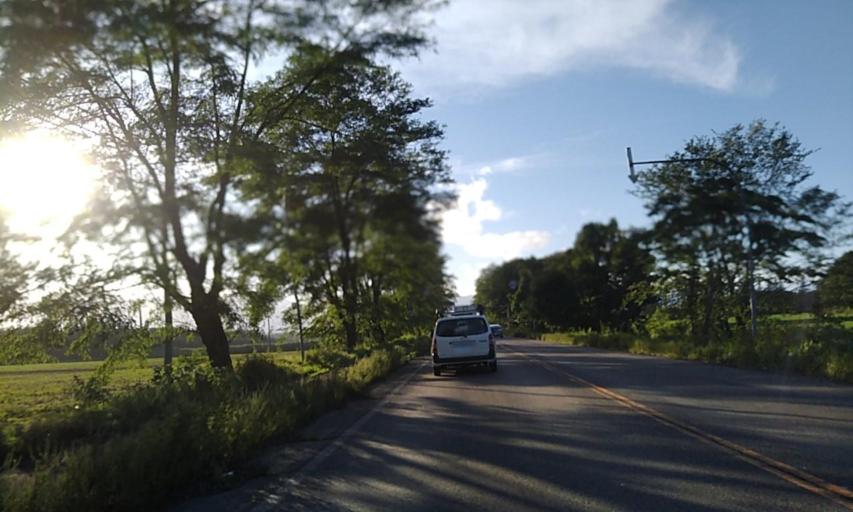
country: JP
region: Hokkaido
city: Obihiro
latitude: 42.9343
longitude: 142.9702
